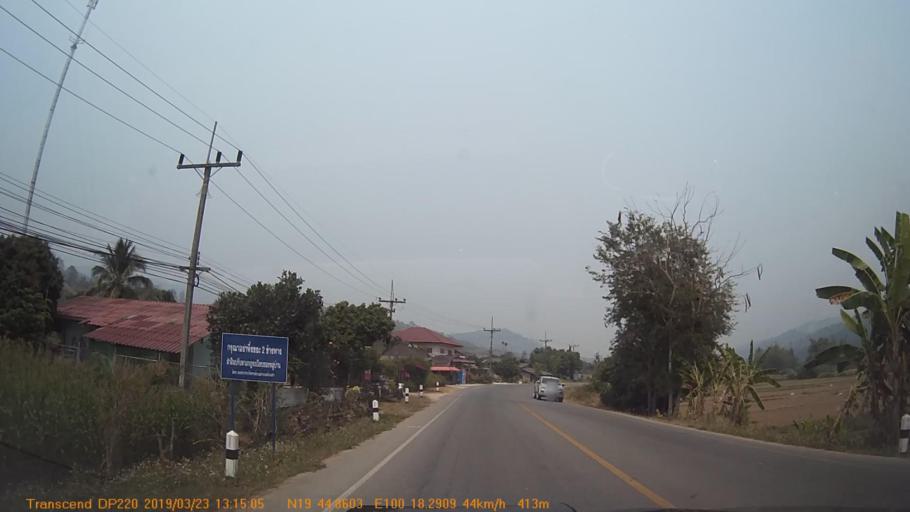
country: TH
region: Chiang Rai
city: Khun Tan
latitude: 19.7479
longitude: 100.3050
